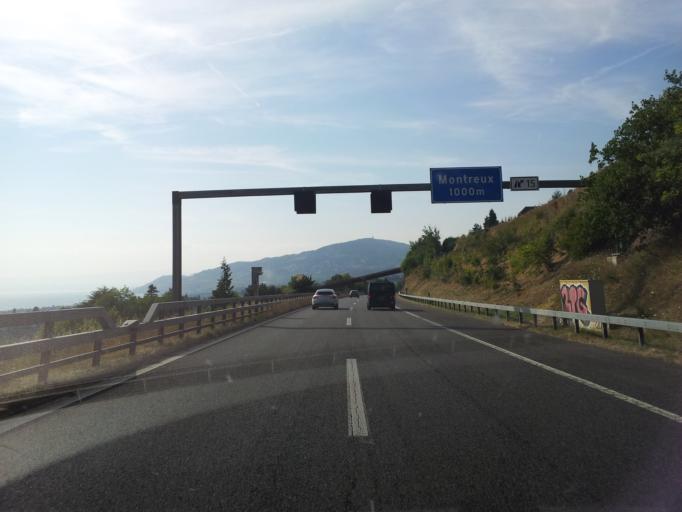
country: CH
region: Vaud
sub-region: Riviera-Pays-d'Enhaut District
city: Le Chatelard
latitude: 46.4437
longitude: 6.9068
